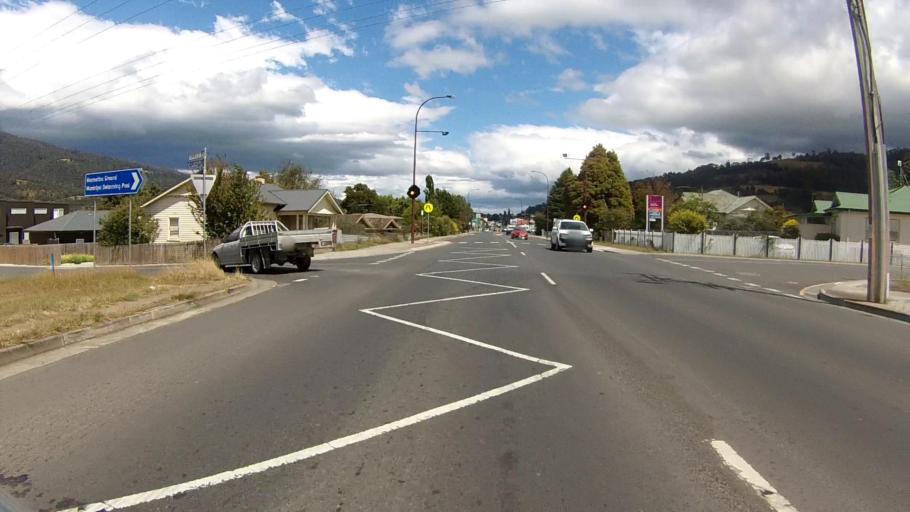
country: AU
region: Tasmania
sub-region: Huon Valley
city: Huonville
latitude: -43.0267
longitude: 147.0507
